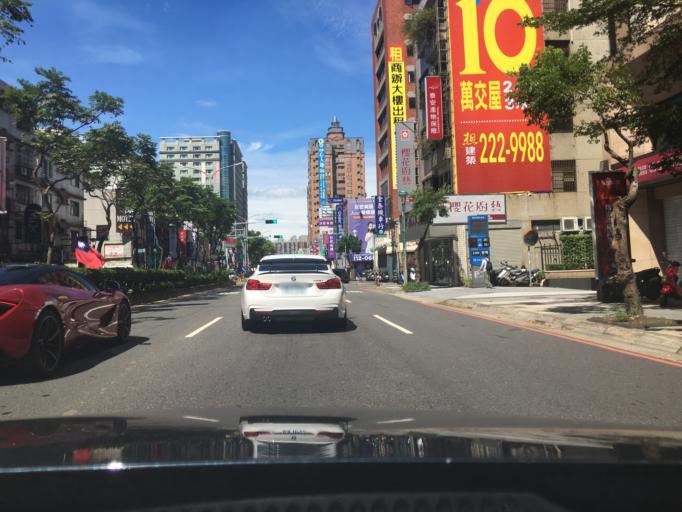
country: TW
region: Taiwan
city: Taoyuan City
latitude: 25.0453
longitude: 121.2934
